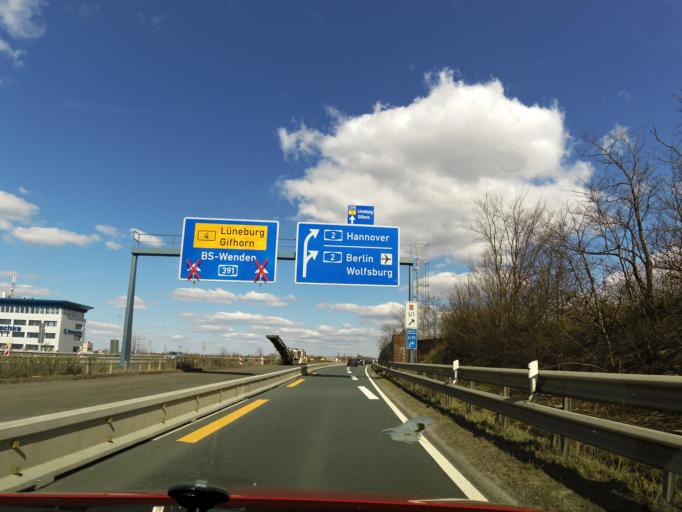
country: DE
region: Lower Saxony
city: Braunschweig
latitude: 52.3105
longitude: 10.5133
